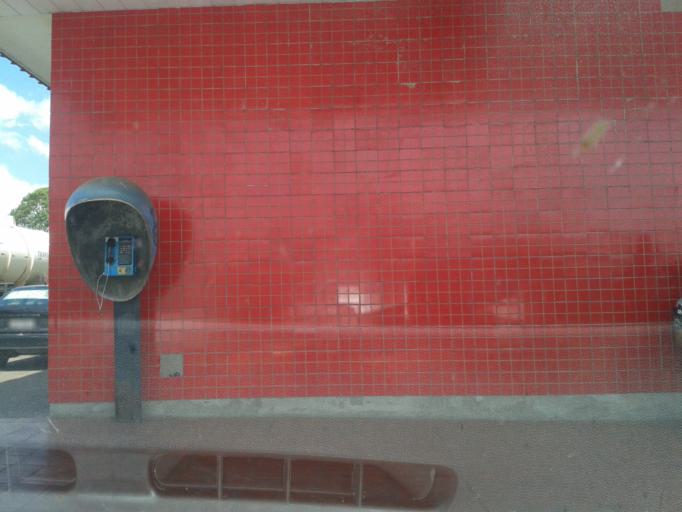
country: BR
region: Minas Gerais
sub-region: Ibia
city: Ibia
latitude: -19.5921
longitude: -46.4928
